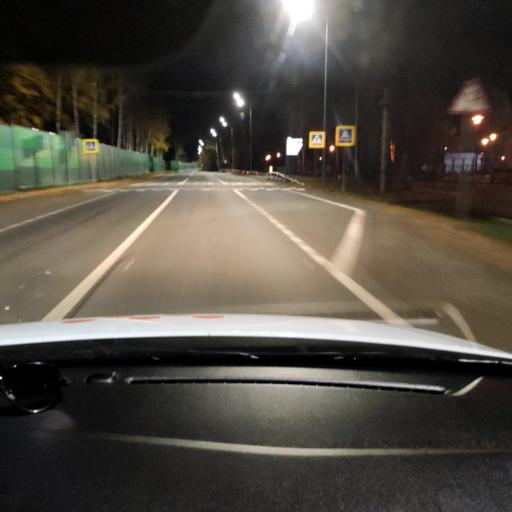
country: RU
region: Tatarstan
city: Verkhniy Uslon
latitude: 55.6246
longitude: 49.0139
